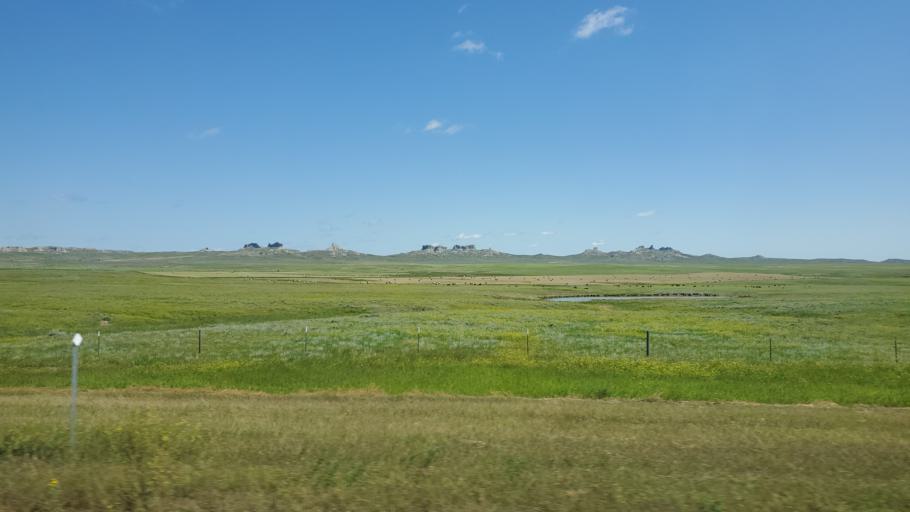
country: US
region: Montana
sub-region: Carter County
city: Ekalaka
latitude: 45.2835
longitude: -104.4362
